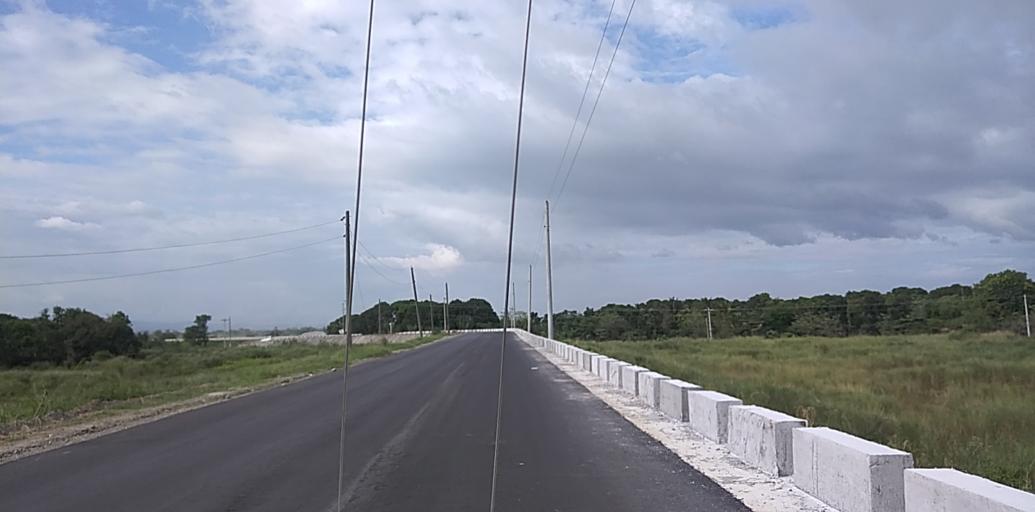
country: PH
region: Central Luzon
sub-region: Province of Pampanga
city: Porac
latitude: 15.0663
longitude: 120.5600
